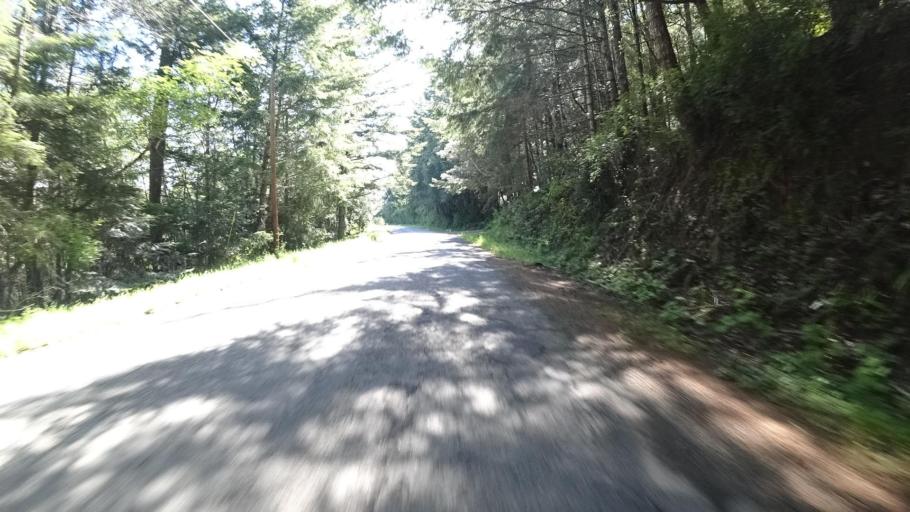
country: US
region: California
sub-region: Humboldt County
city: Rio Dell
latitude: 40.3110
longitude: -124.2784
